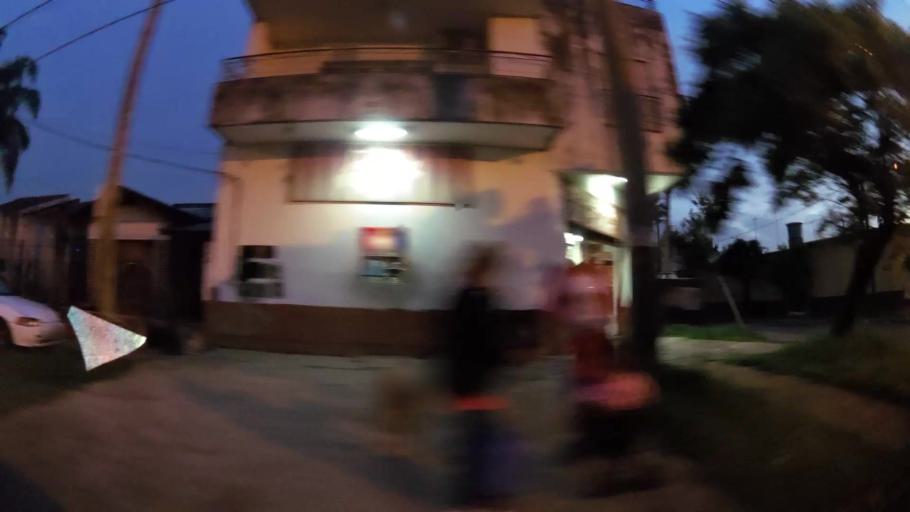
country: AR
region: Buenos Aires
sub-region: Partido de Lomas de Zamora
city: Lomas de Zamora
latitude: -34.7440
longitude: -58.3638
